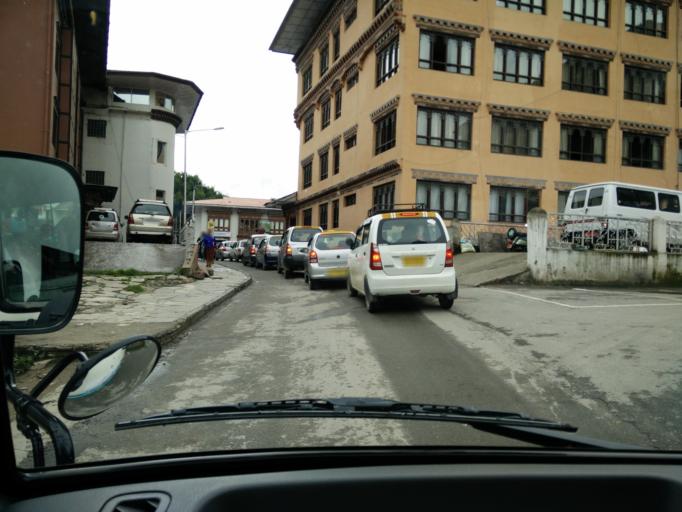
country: BT
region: Thimphu
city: Thimphu
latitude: 27.4719
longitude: 89.6379
